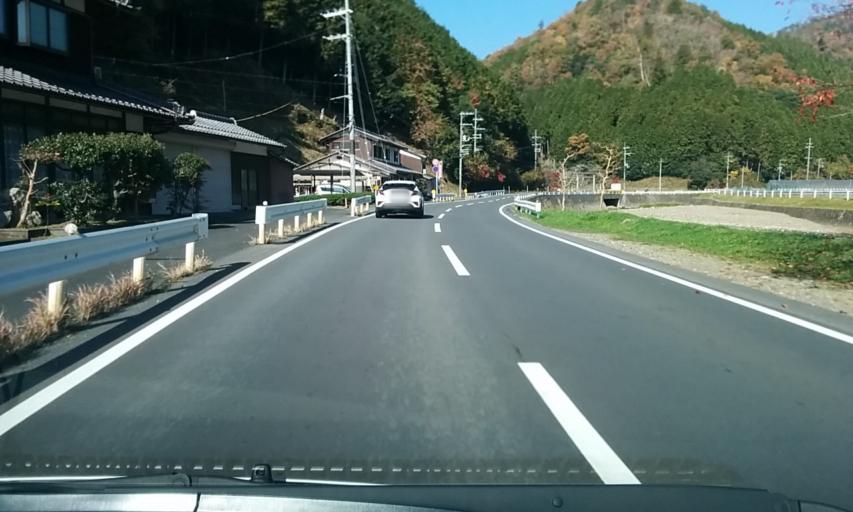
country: JP
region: Kyoto
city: Kameoka
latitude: 35.1963
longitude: 135.5218
